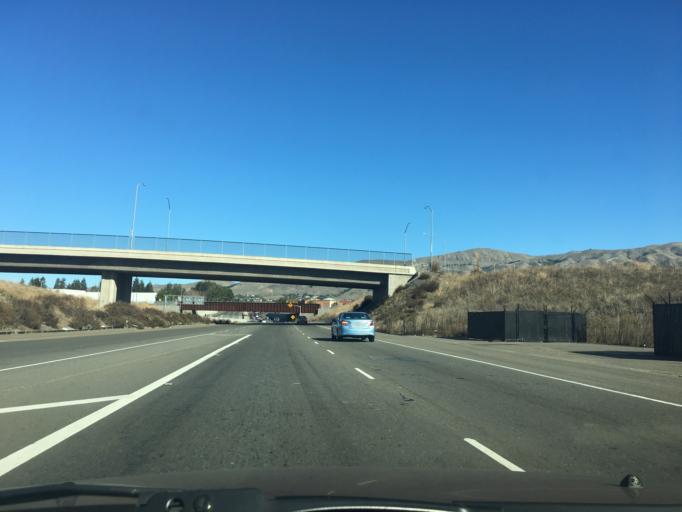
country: US
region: California
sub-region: Santa Clara County
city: Milpitas
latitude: 37.4852
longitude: -121.9340
